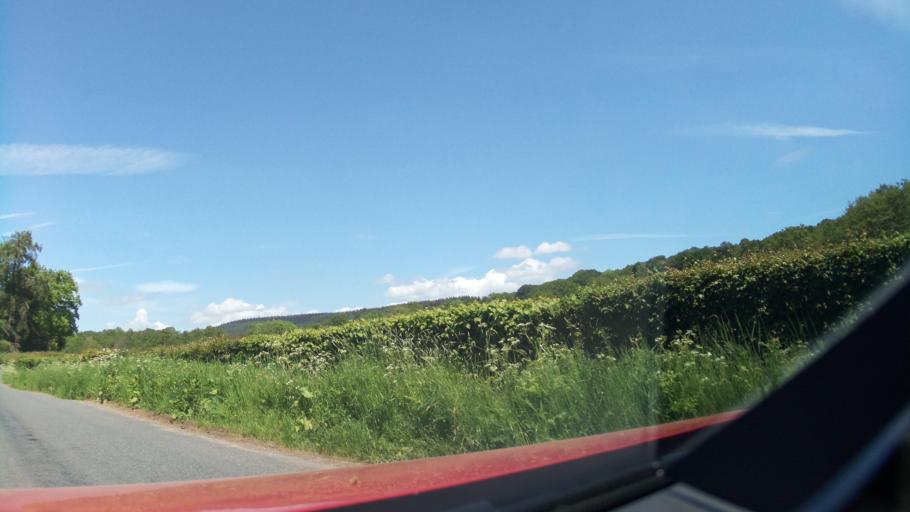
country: GB
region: Wales
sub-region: Monmouthshire
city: Caldicot
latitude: 51.6507
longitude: -2.7558
